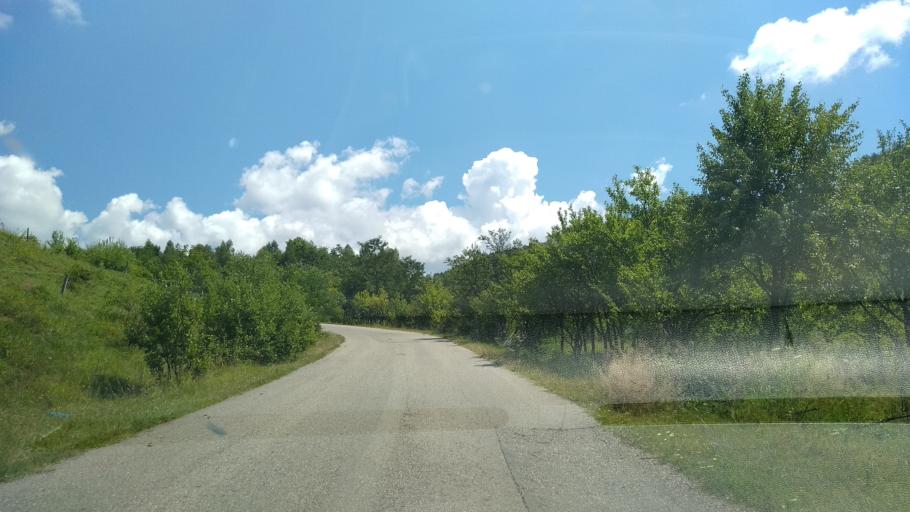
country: RO
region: Hunedoara
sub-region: Comuna Orastioara de Sus
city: Orastioara de Sus
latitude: 45.7068
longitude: 23.1408
